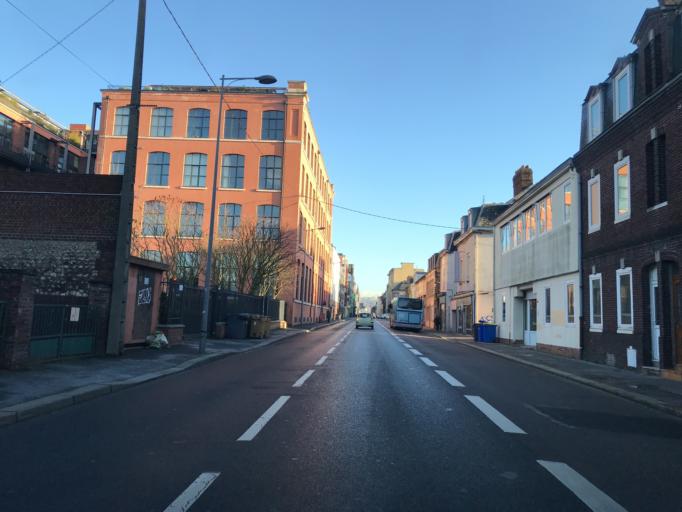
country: FR
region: Haute-Normandie
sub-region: Departement de la Seine-Maritime
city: Sotteville-les-Rouen
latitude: 49.4244
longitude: 1.0817
